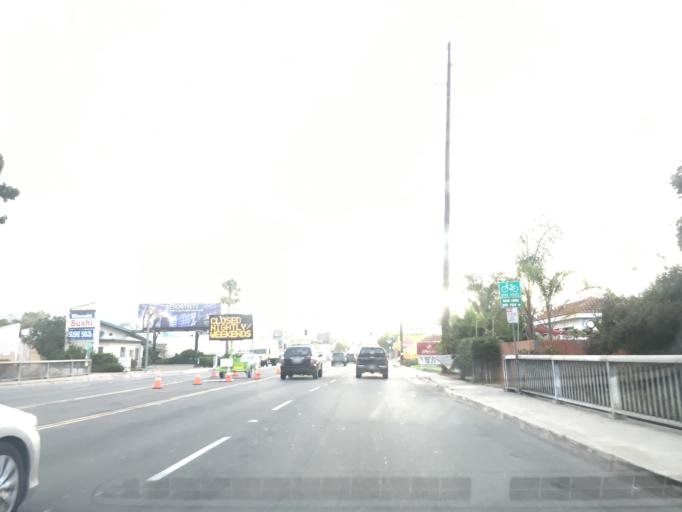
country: US
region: California
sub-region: San Diego County
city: La Jolla
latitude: 32.8052
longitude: -117.2226
